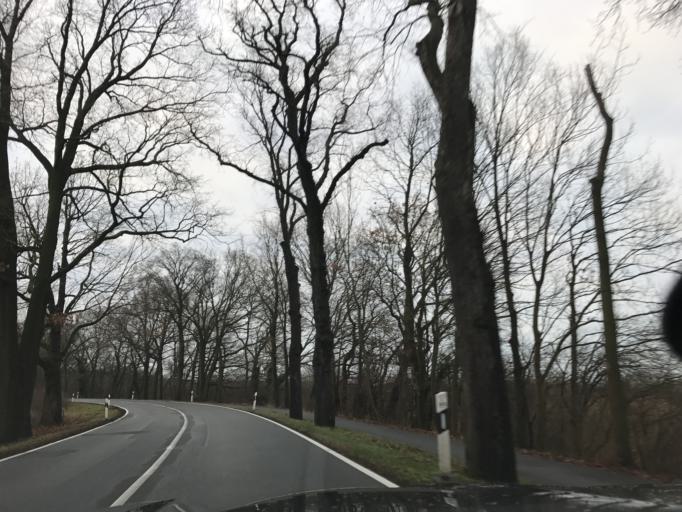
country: DE
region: Brandenburg
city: Werder
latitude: 52.3770
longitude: 12.9547
